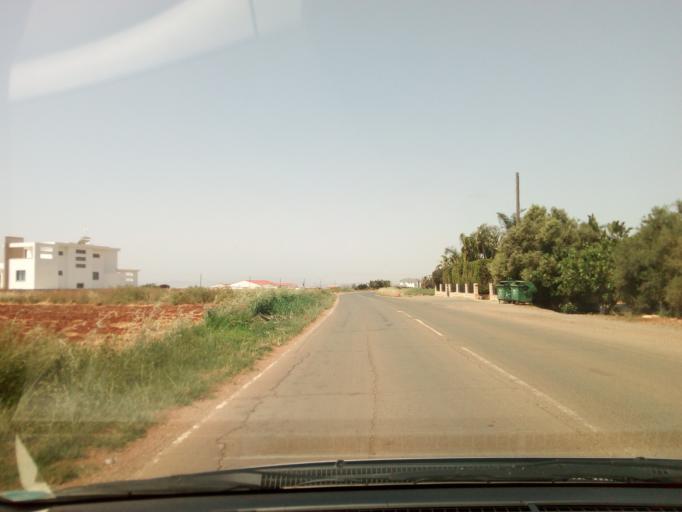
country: CY
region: Ammochostos
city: Avgorou
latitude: 34.9812
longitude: 33.8283
